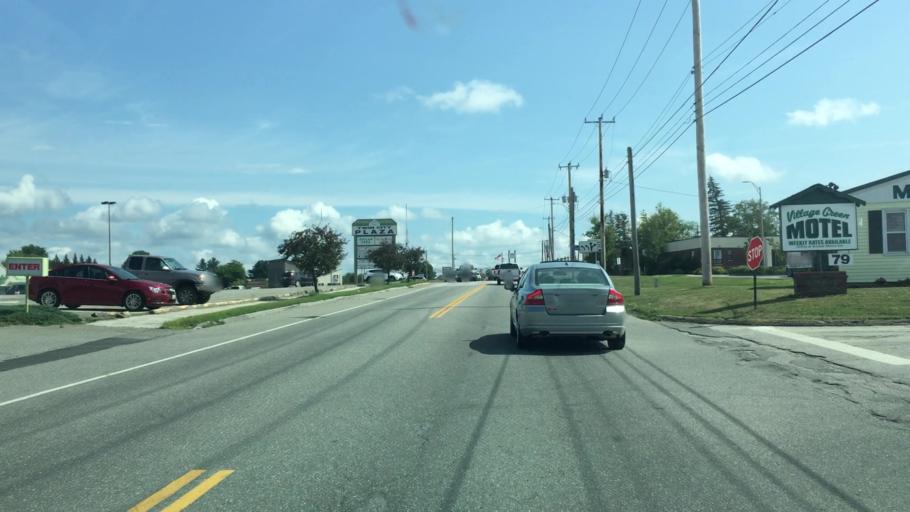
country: US
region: Maine
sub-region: Penobscot County
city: Brewer
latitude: 44.7866
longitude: -68.7538
